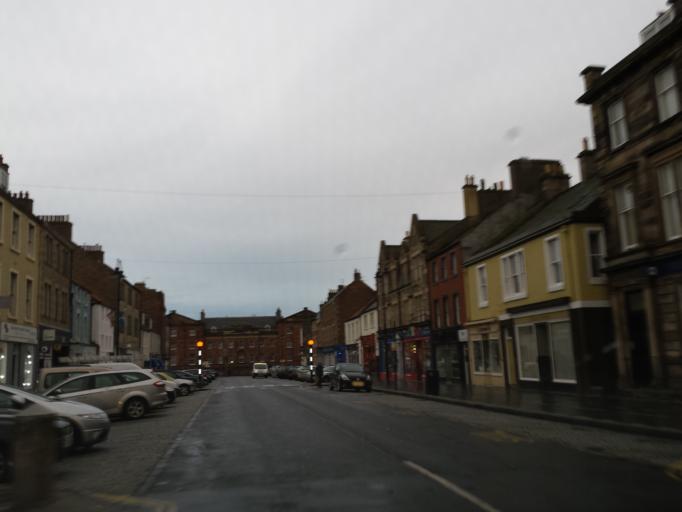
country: GB
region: Scotland
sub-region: East Lothian
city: Dunbar
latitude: 56.0025
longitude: -2.5163
